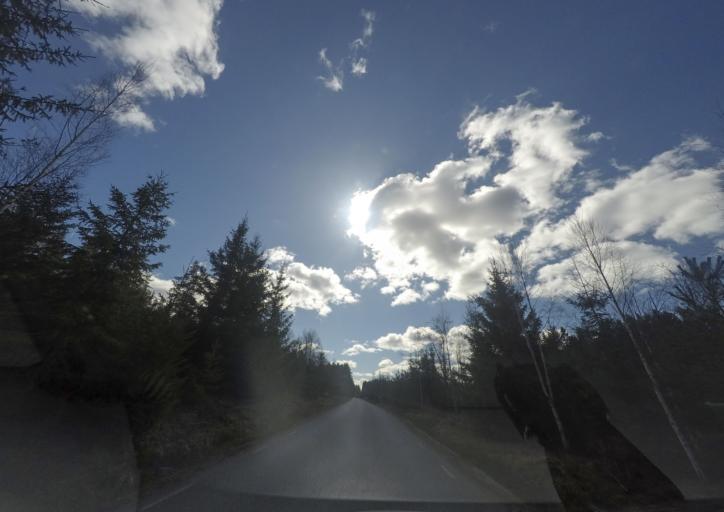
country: SE
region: OEstergoetland
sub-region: Norrkopings Kommun
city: Krokek
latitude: 58.7909
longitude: 16.4572
